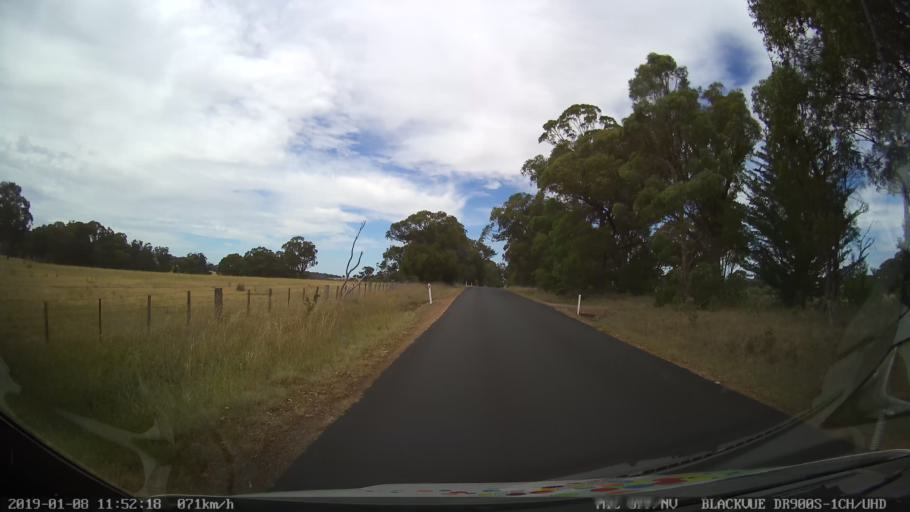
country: AU
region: New South Wales
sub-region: Armidale Dumaresq
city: Armidale
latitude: -30.4023
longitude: 151.5606
